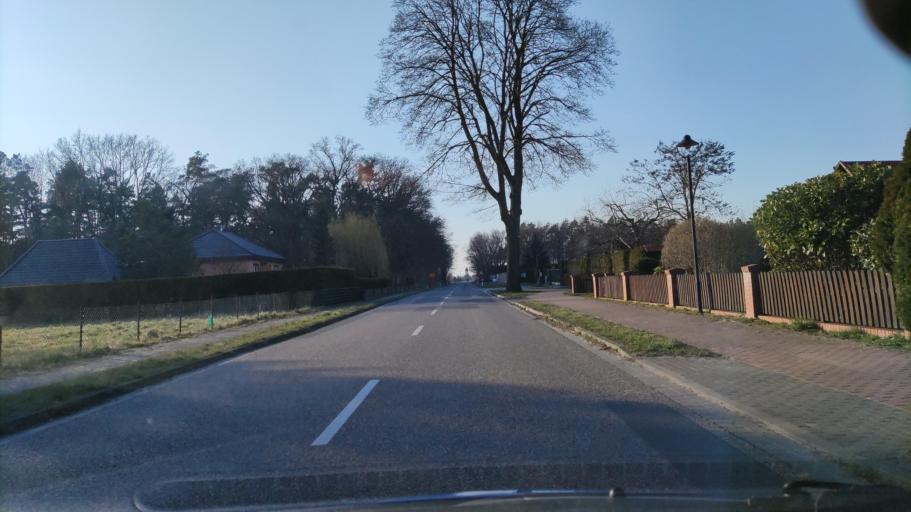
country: DE
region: Saxony-Anhalt
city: Seehausen
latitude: 52.9256
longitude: 11.6847
